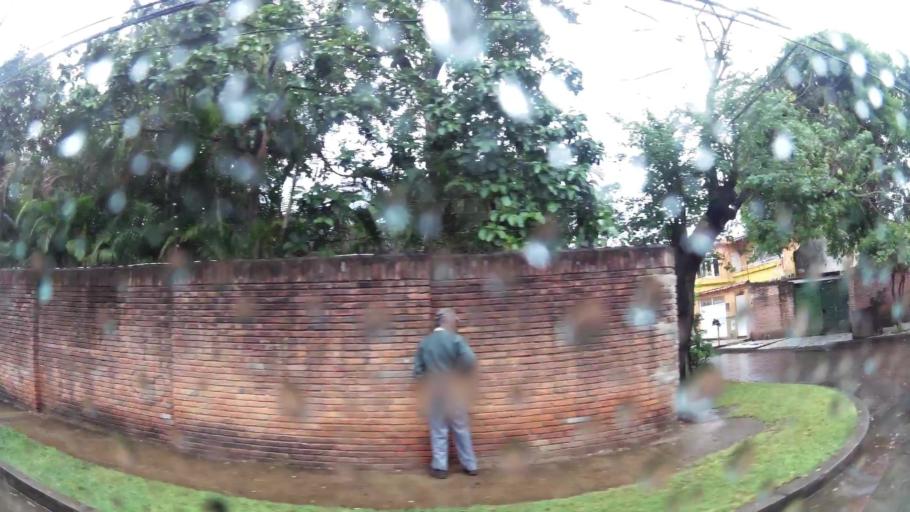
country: BO
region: Santa Cruz
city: Santa Cruz de la Sierra
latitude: -17.7903
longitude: -63.2146
